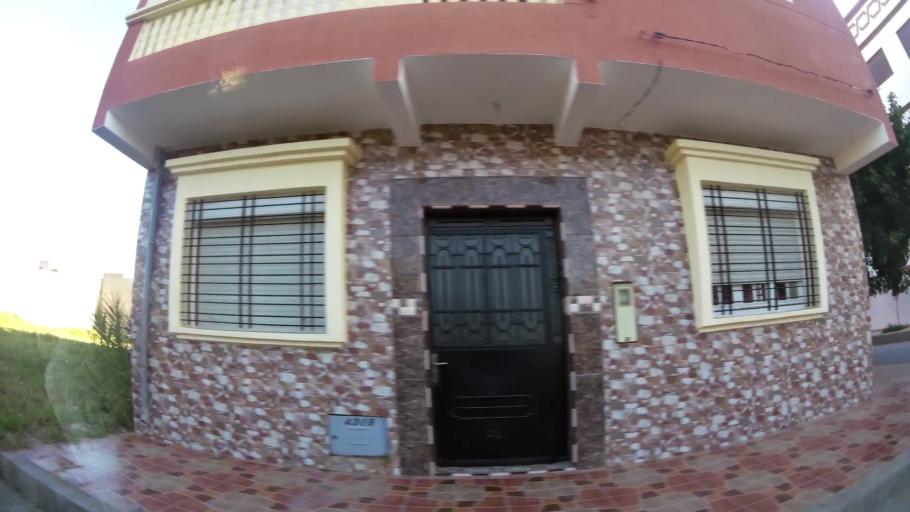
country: MA
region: Oriental
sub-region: Berkane-Taourirt
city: Madagh
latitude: 35.0853
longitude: -2.2434
